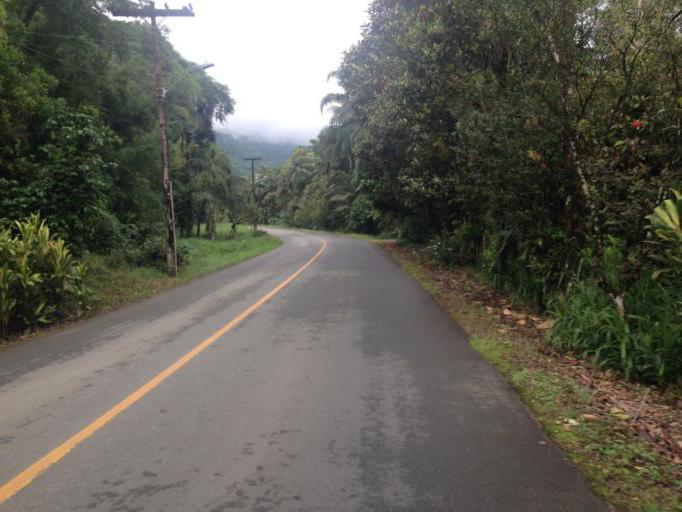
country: BR
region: Santa Catarina
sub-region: Joinville
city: Joinville
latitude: -26.1286
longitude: -48.9224
